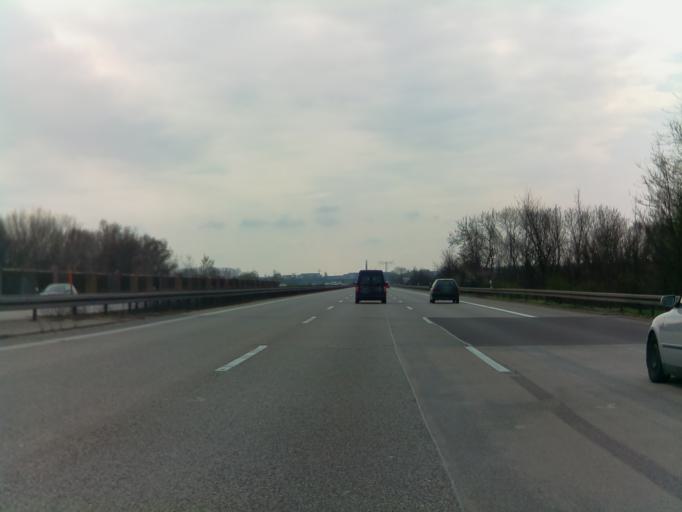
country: DE
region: Saxony-Anhalt
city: Gunthersdorf
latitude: 51.3727
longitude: 12.1868
